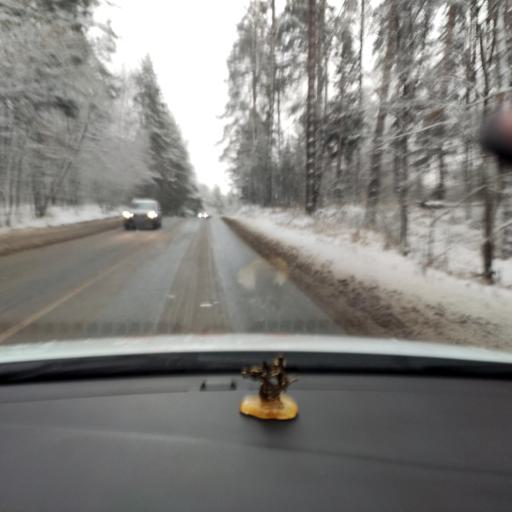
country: RU
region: Tatarstan
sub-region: Zelenodol'skiy Rayon
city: Zelenodolsk
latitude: 55.8625
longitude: 48.5347
